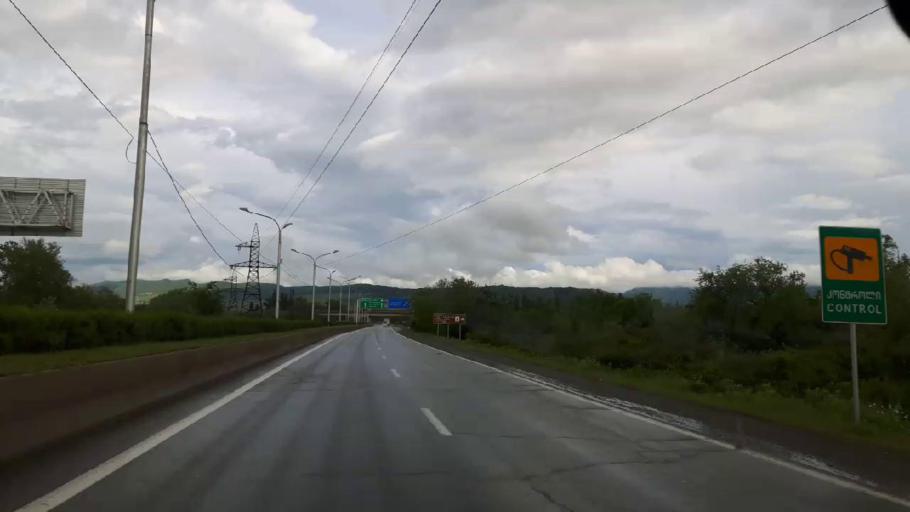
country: GE
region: Shida Kartli
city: Kaspi
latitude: 41.9151
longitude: 44.5564
